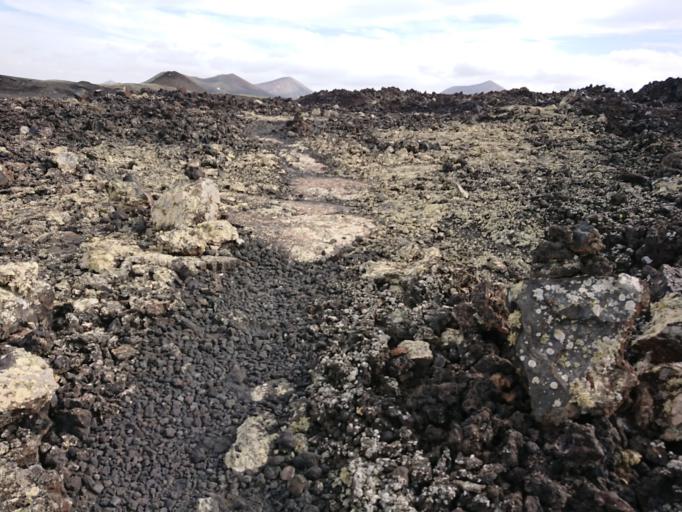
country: ES
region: Canary Islands
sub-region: Provincia de Las Palmas
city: Tinajo
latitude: 29.0114
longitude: -13.6766
